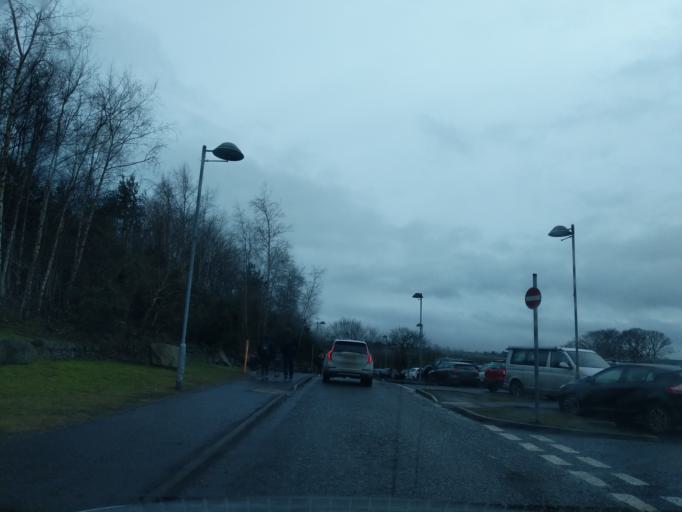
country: GB
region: Scotland
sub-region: Edinburgh
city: Newbridge
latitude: 55.9238
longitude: -3.3992
